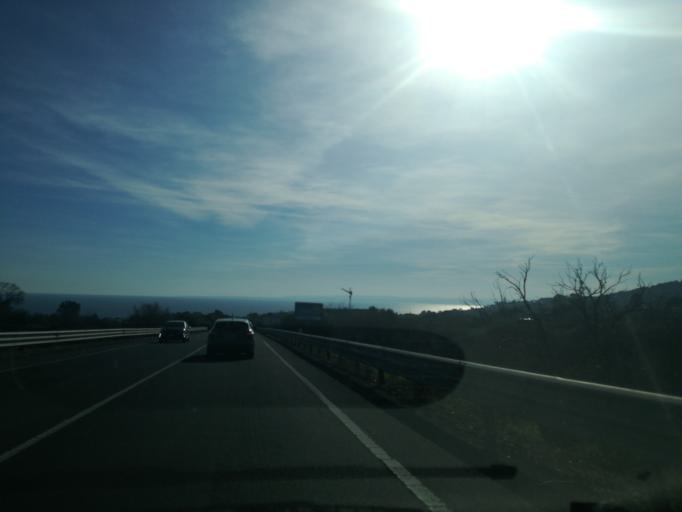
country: IT
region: Sicily
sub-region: Catania
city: Vambolieri
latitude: 37.5889
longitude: 15.1691
